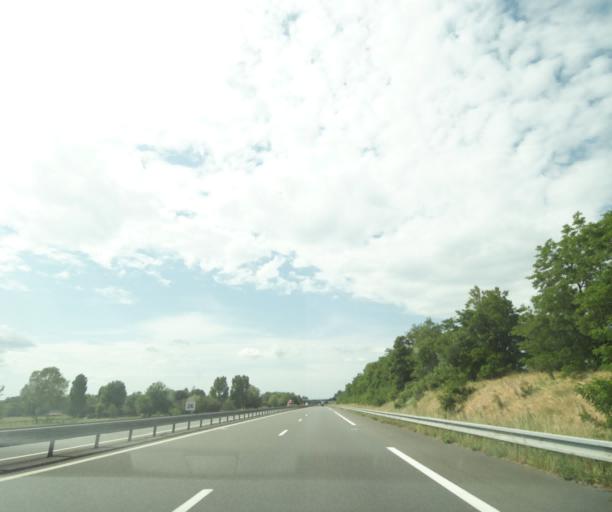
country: FR
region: Pays de la Loire
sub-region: Departement de Maine-et-Loire
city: Jumelles
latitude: 47.3938
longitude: -0.1099
